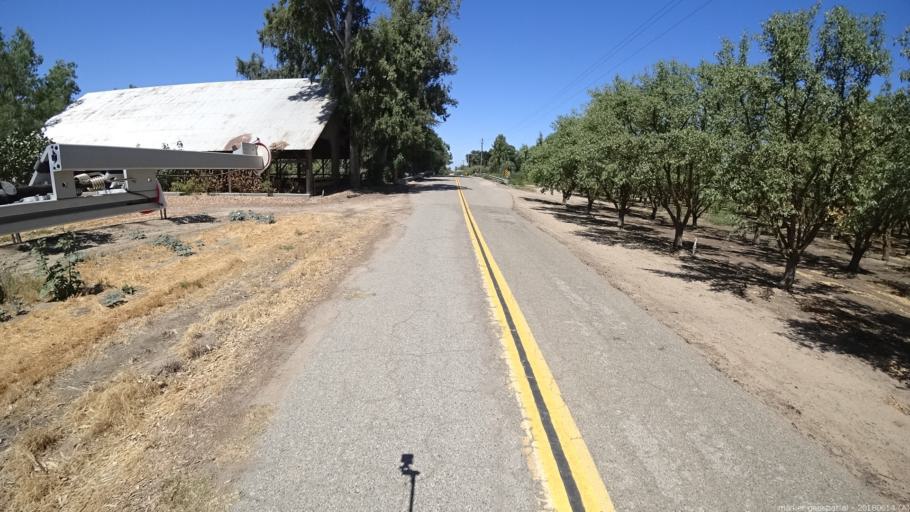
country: US
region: California
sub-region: Madera County
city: Fairmead
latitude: 37.0038
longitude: -120.2453
